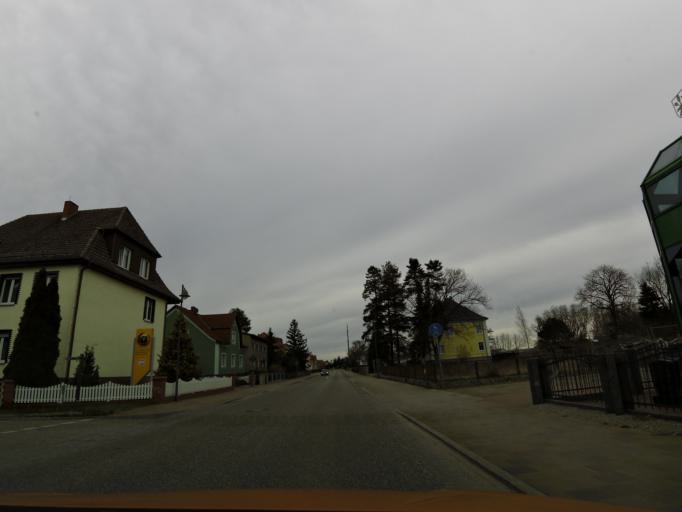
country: DE
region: Brandenburg
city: Bruck
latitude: 52.1877
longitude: 12.7575
